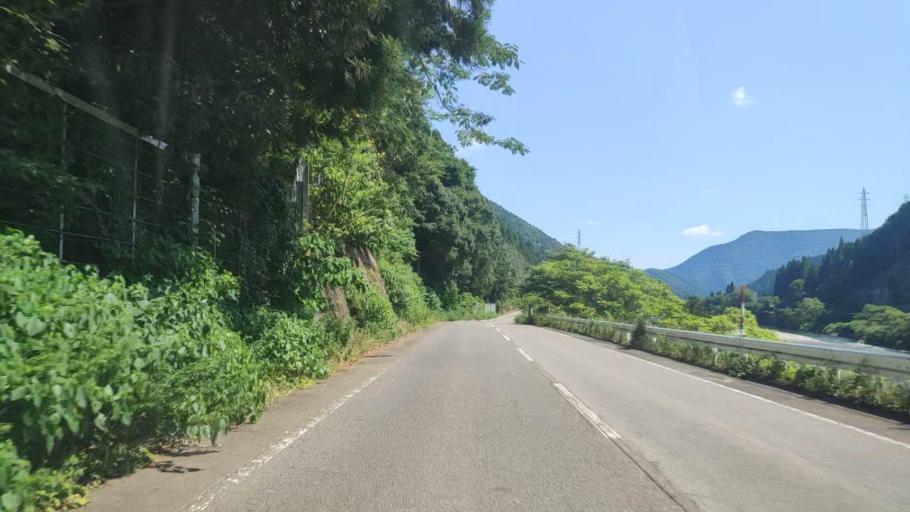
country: JP
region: Gifu
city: Godo
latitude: 35.6098
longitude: 136.6269
